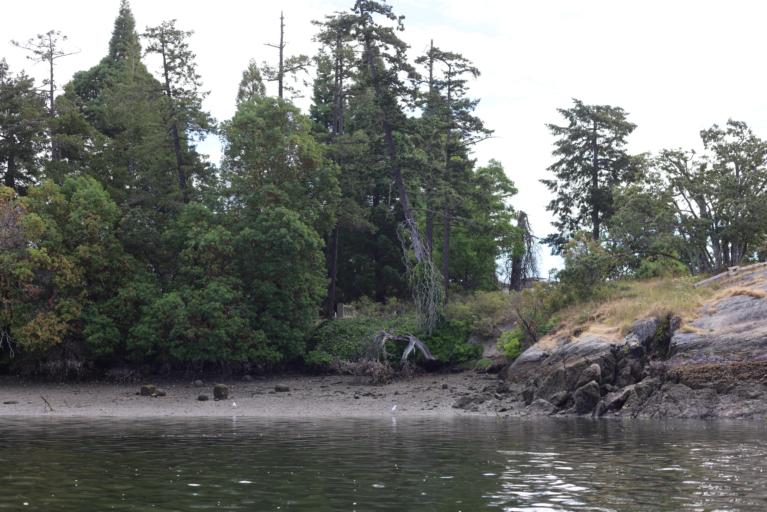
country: CA
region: British Columbia
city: Victoria
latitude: 48.4446
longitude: -123.3958
